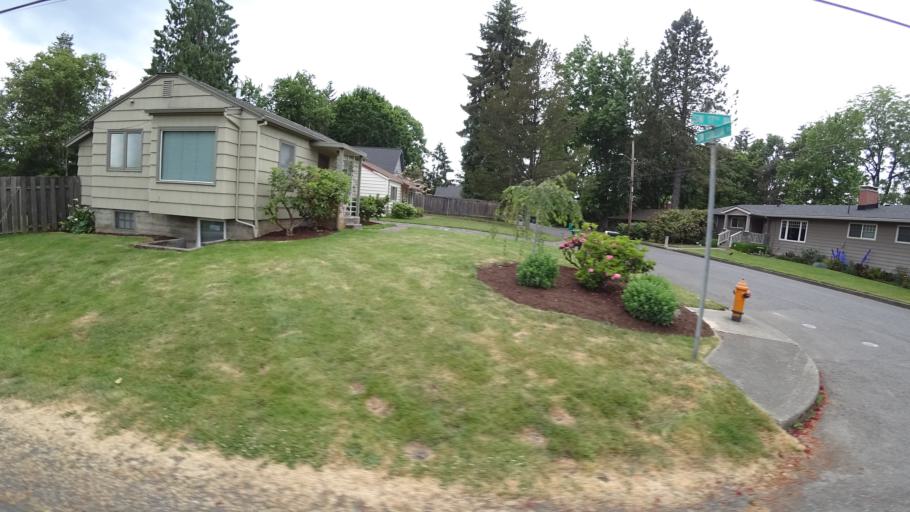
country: US
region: Oregon
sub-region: Clackamas County
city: Lake Oswego
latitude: 45.4610
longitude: -122.6952
